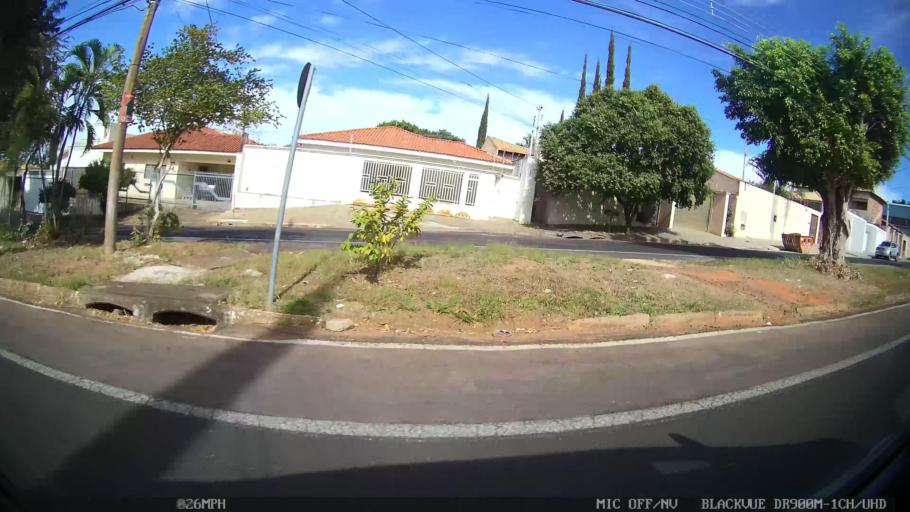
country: BR
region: Sao Paulo
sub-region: Catanduva
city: Catanduva
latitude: -21.1169
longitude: -48.9626
